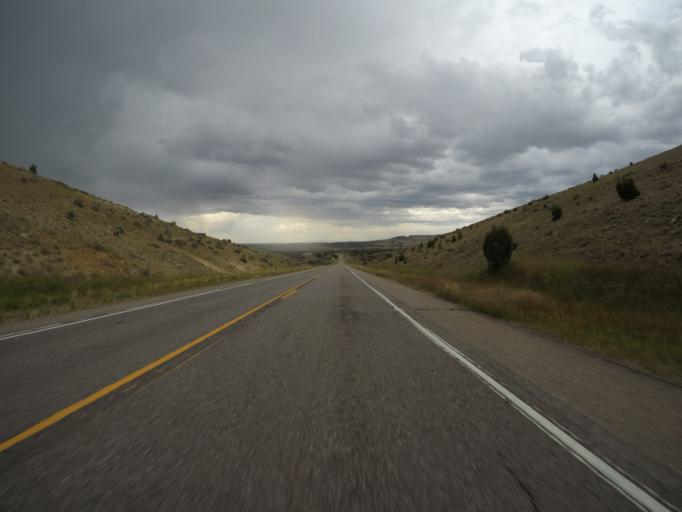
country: US
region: Colorado
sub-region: Rio Blanco County
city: Rangely
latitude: 40.3773
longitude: -108.3693
